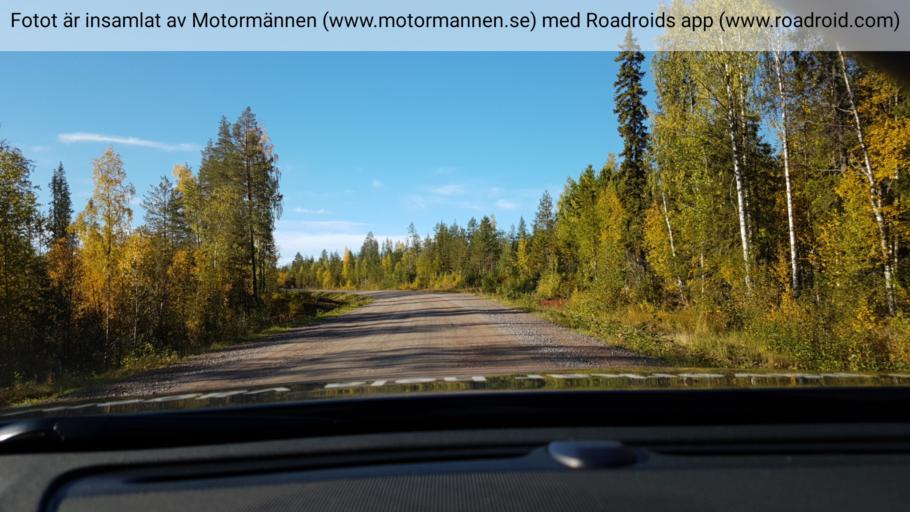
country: SE
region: Norrbotten
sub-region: Alvsbyns Kommun
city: AElvsbyn
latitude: 66.2642
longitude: 20.9723
